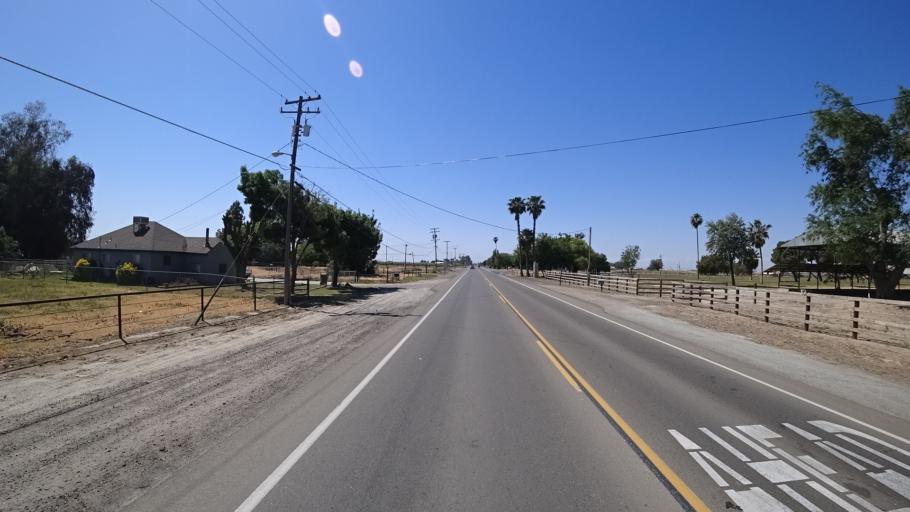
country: US
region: California
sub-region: Kings County
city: Lemoore
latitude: 36.2560
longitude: -119.7808
